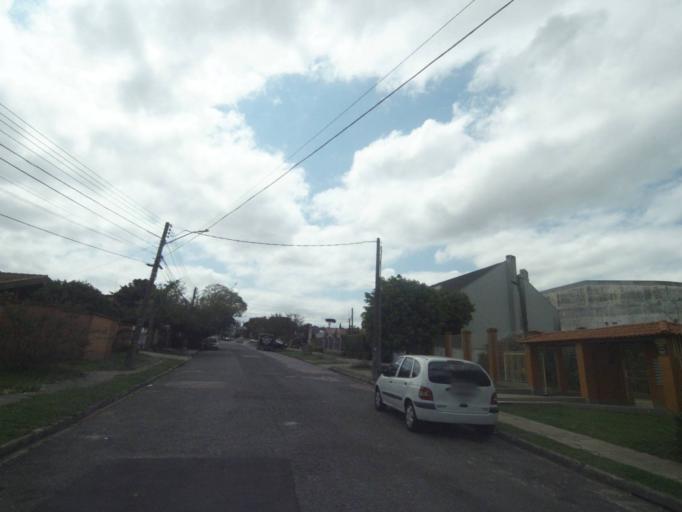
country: BR
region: Parana
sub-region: Pinhais
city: Pinhais
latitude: -25.4133
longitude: -49.2261
